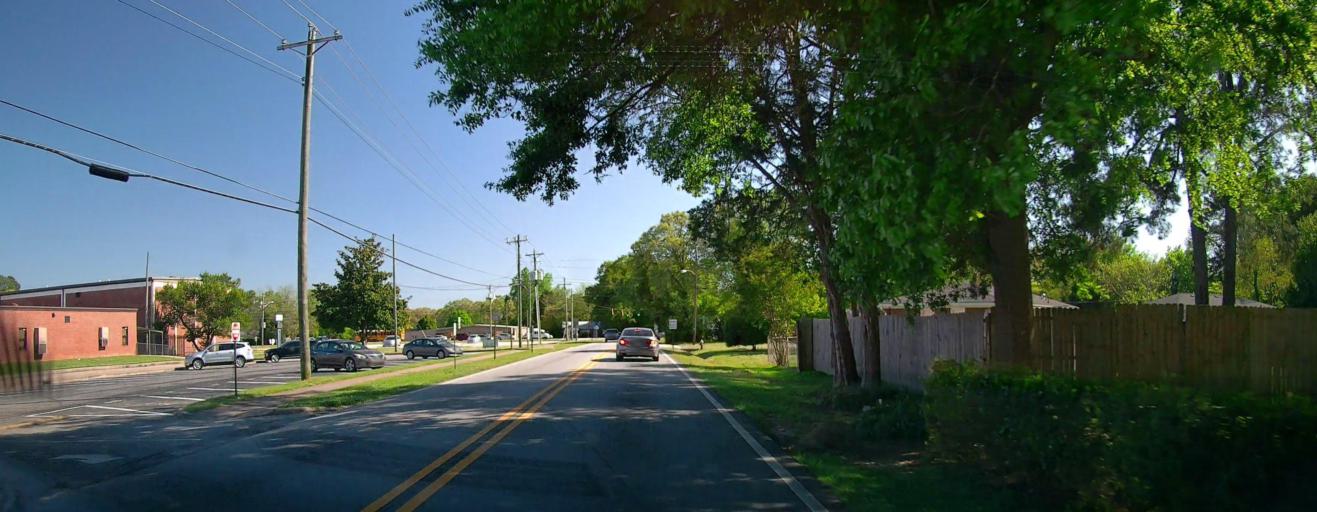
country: US
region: Georgia
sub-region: Houston County
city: Warner Robins
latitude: 32.6280
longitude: -83.6321
